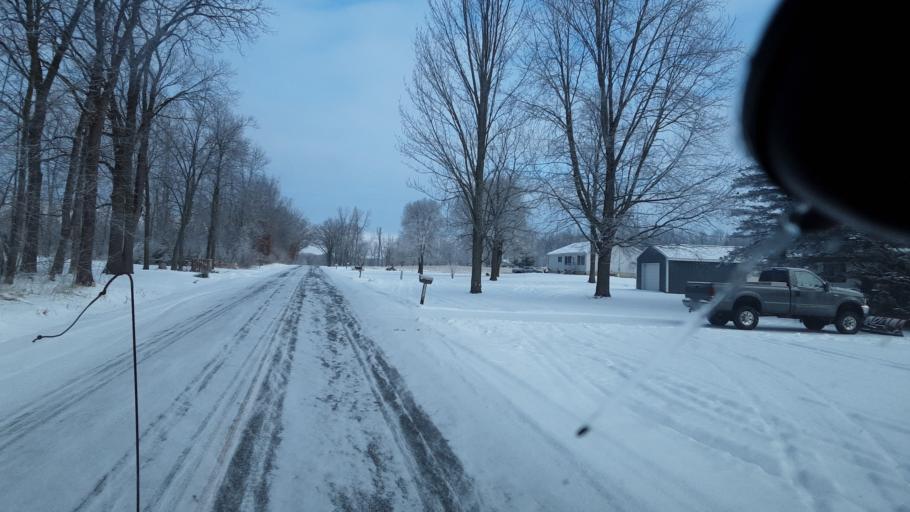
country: US
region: Michigan
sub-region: Ingham County
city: Leslie
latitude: 42.4122
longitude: -84.4823
